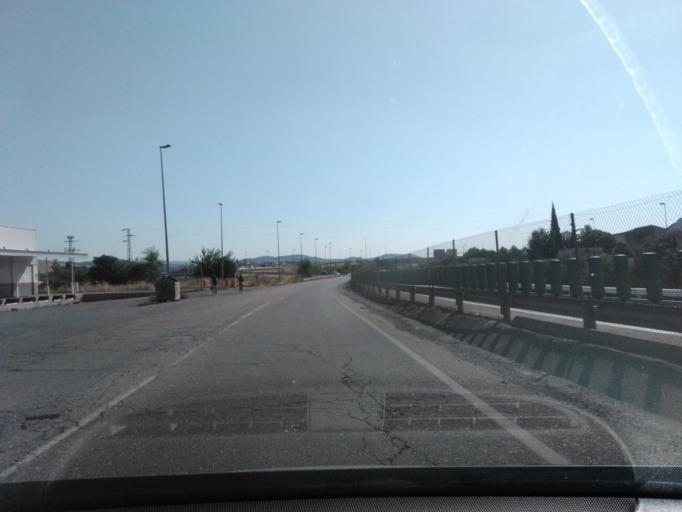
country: ES
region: Andalusia
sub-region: Provincia de Jaen
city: La Carolina
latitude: 38.2803
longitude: -3.5983
